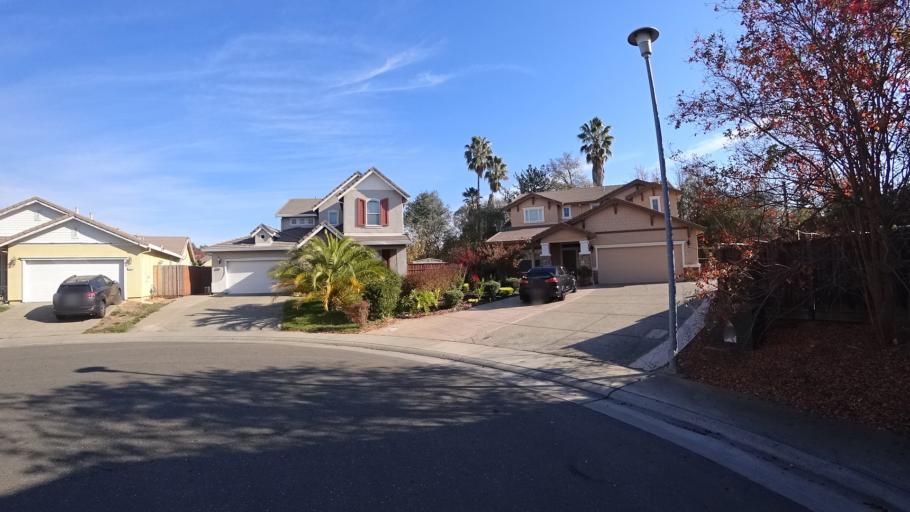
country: US
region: California
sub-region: Sacramento County
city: Citrus Heights
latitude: 38.6858
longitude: -121.2952
